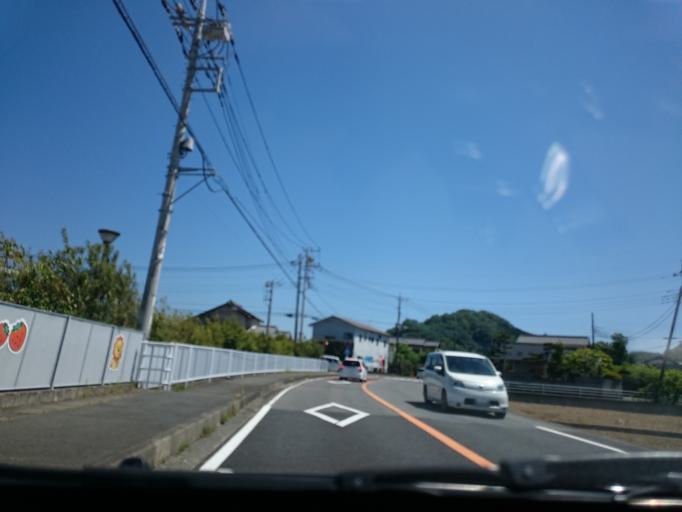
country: JP
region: Shizuoka
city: Mishima
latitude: 35.0733
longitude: 138.9305
